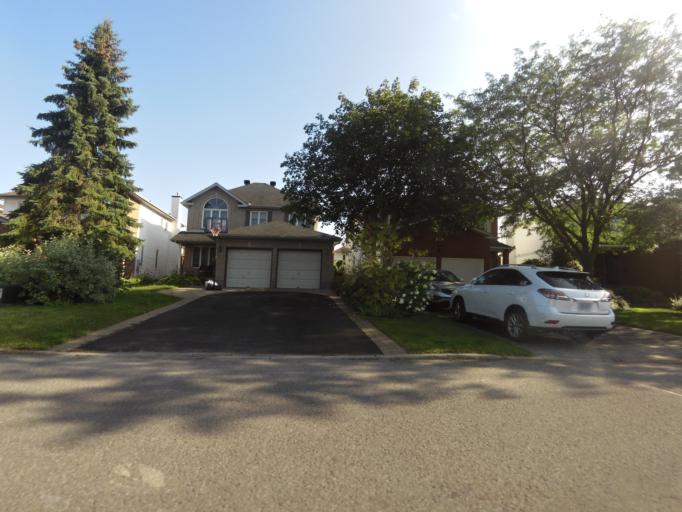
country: CA
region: Ontario
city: Clarence-Rockland
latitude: 45.4815
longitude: -75.4828
